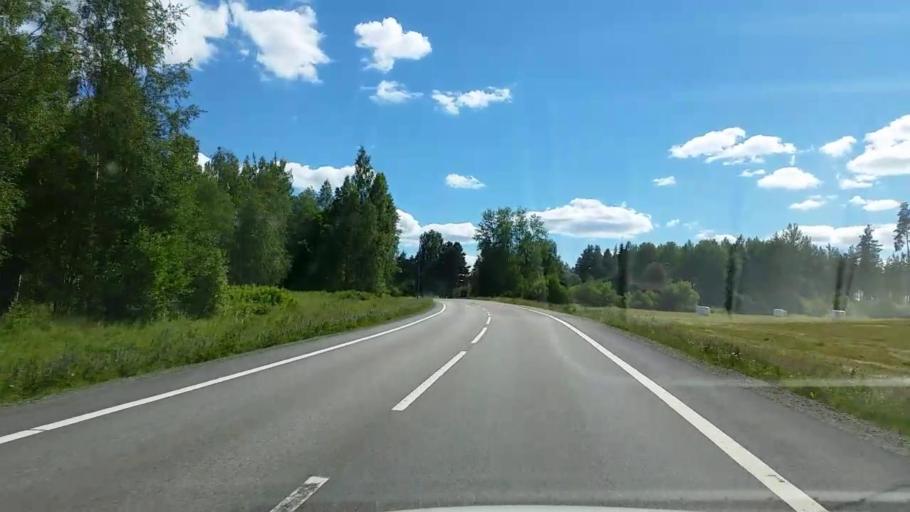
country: SE
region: Dalarna
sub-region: Faluns Kommun
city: Svardsjo
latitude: 60.8298
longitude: 15.7602
